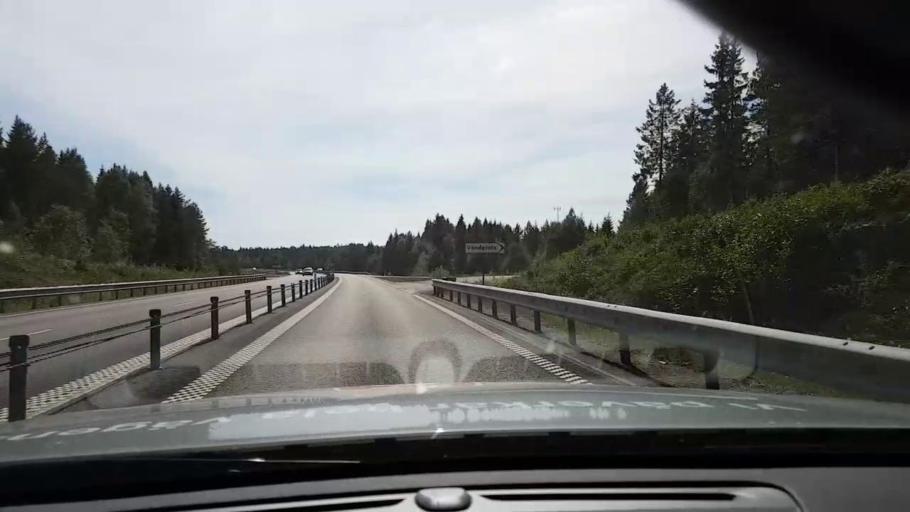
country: SE
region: Vaesternorrland
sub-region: OErnskoeldsviks Kommun
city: Husum
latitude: 63.3952
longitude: 19.1959
